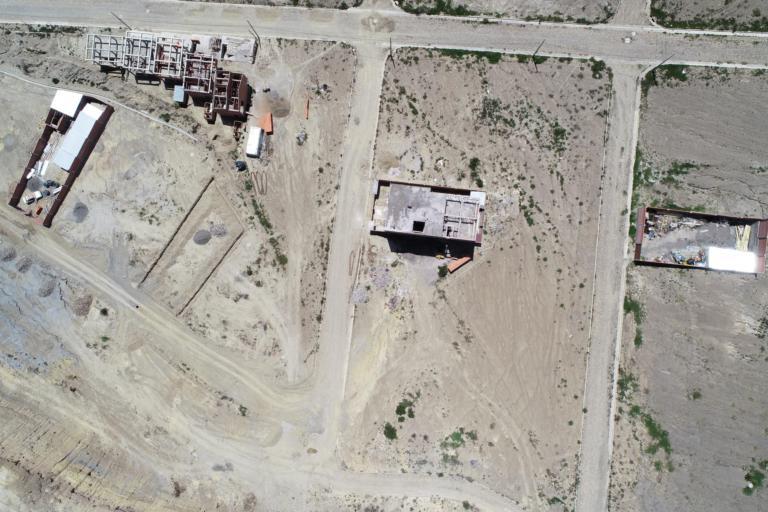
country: BO
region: La Paz
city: La Paz
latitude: -16.5234
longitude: -68.0480
